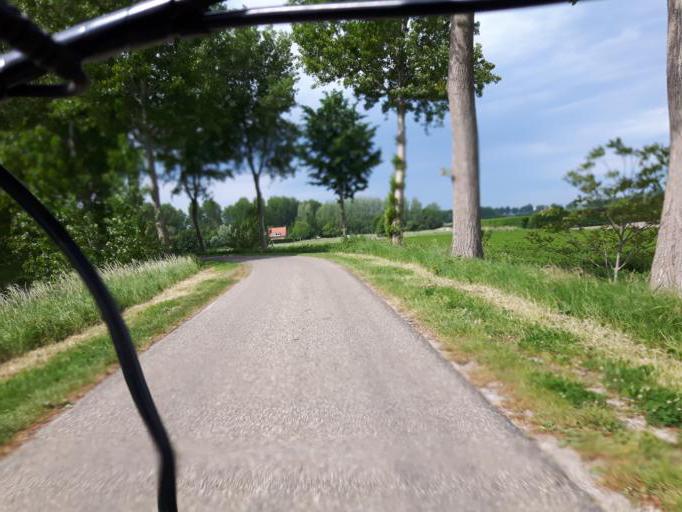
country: NL
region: Zeeland
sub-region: Gemeente Borsele
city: Borssele
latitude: 51.4274
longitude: 3.7832
